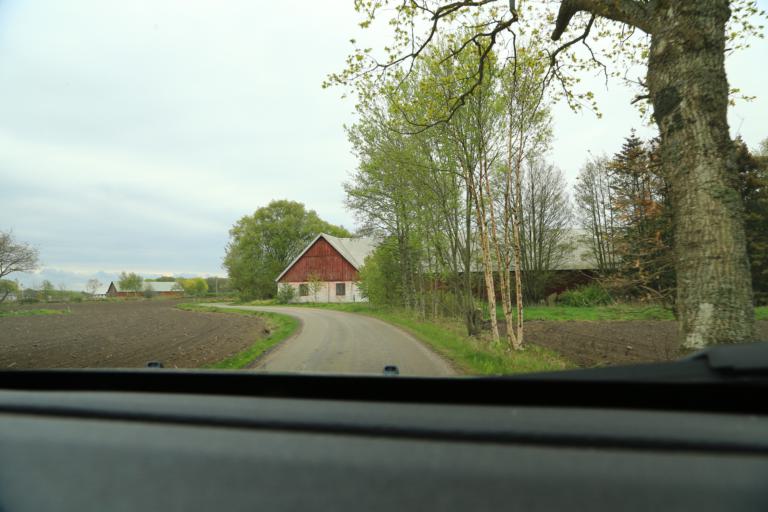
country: SE
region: Halland
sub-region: Varbergs Kommun
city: Traslovslage
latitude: 57.0622
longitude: 12.3212
